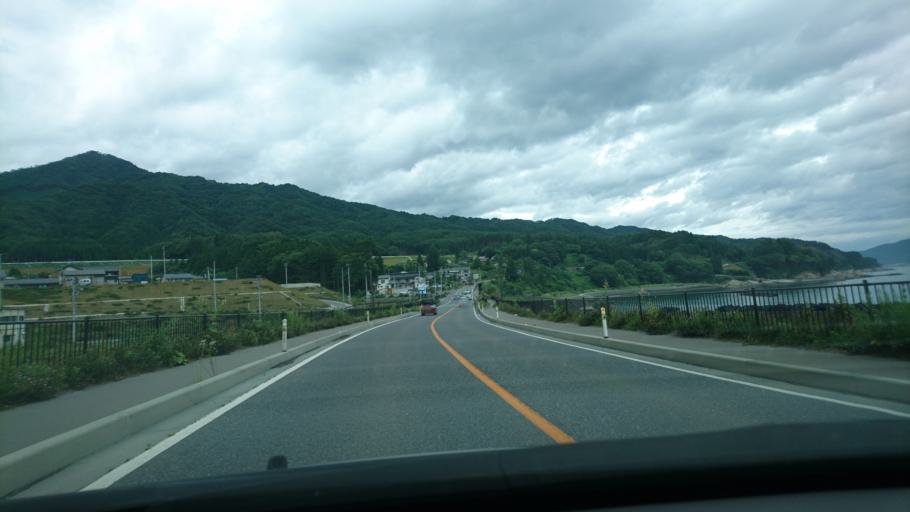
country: JP
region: Iwate
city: Otsuchi
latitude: 39.3823
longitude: 141.9374
